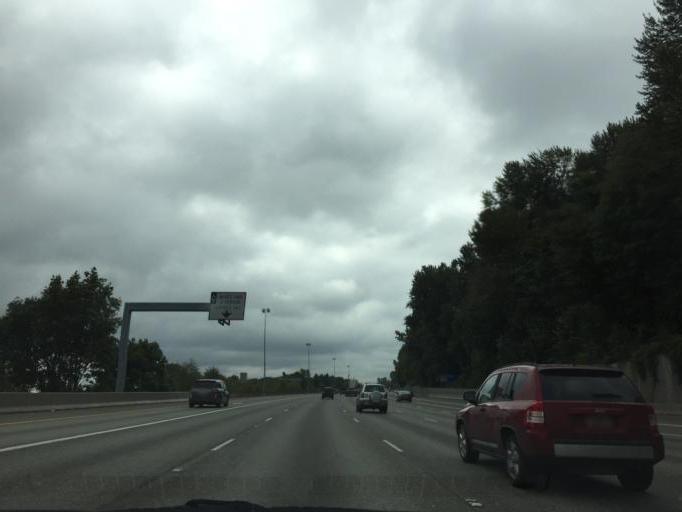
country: US
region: Washington
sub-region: King County
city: Tukwila
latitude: 47.4552
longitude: -122.2645
